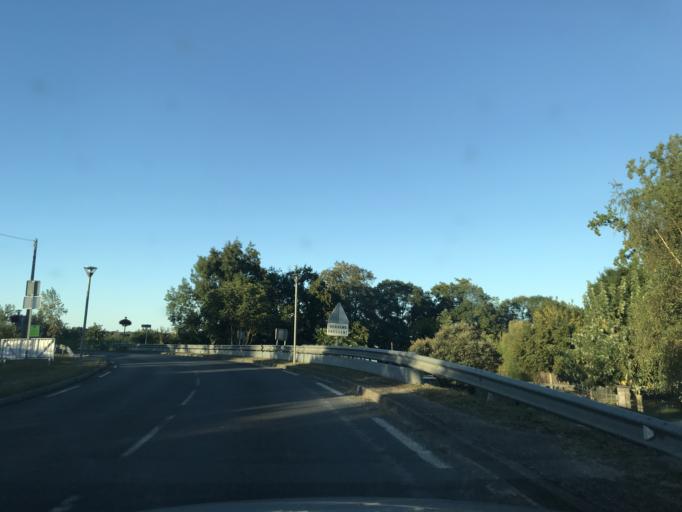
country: FR
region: Aquitaine
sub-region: Departement de la Gironde
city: Saint-Medard-de-Guizieres
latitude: 45.0192
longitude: -0.0550
